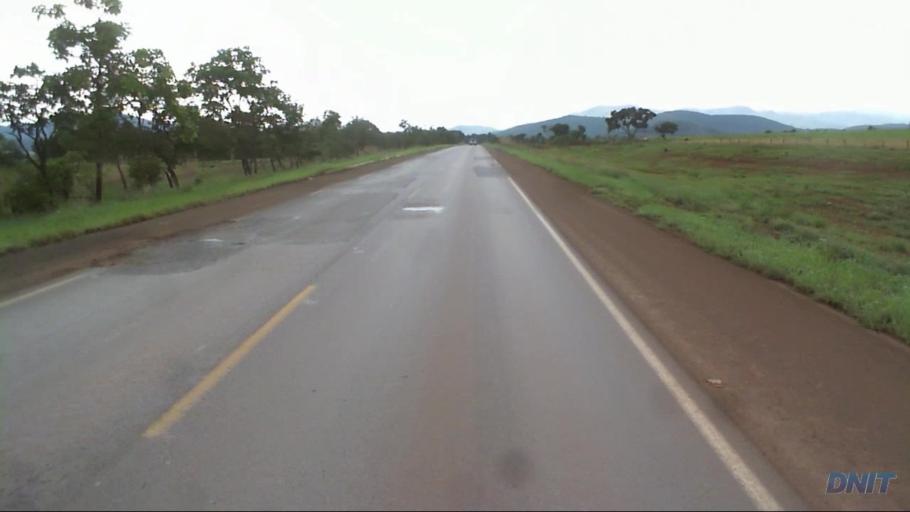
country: BR
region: Goias
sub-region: Barro Alto
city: Barro Alto
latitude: -14.8597
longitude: -49.0203
